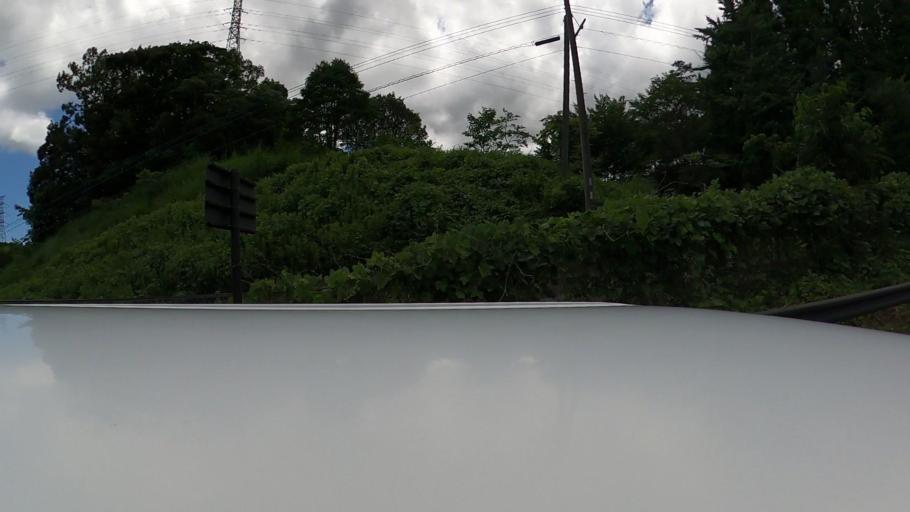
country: JP
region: Miyazaki
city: Nobeoka
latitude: 32.5834
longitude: 131.5161
